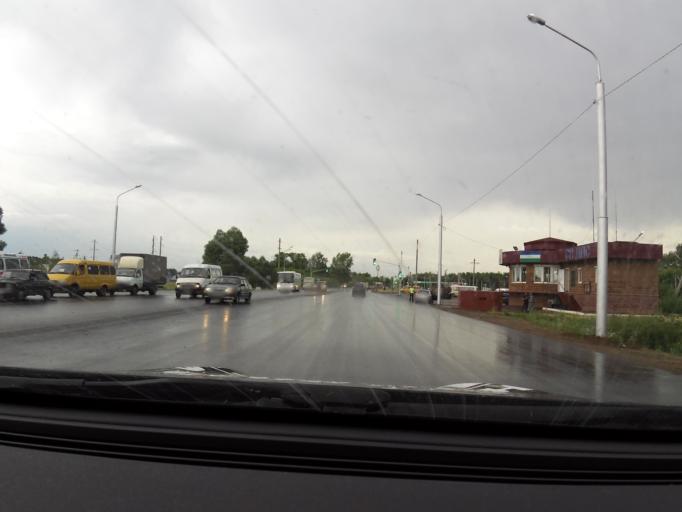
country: RU
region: Bashkortostan
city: Mikhaylovka
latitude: 54.8008
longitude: 55.8601
